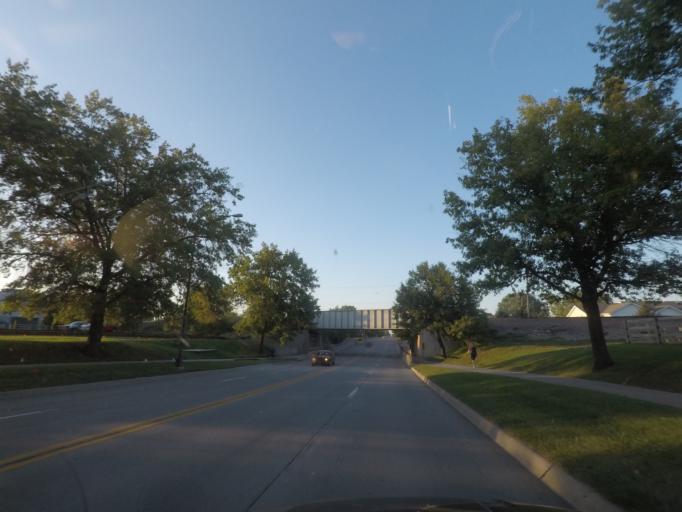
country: US
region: Iowa
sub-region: Story County
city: Ames
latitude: 42.0317
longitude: -93.6447
